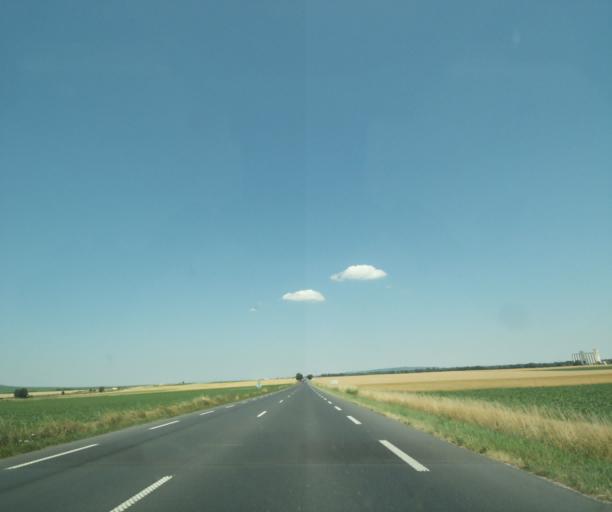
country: FR
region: Champagne-Ardenne
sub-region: Departement de la Marne
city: Verzy
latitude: 49.1493
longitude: 4.2138
